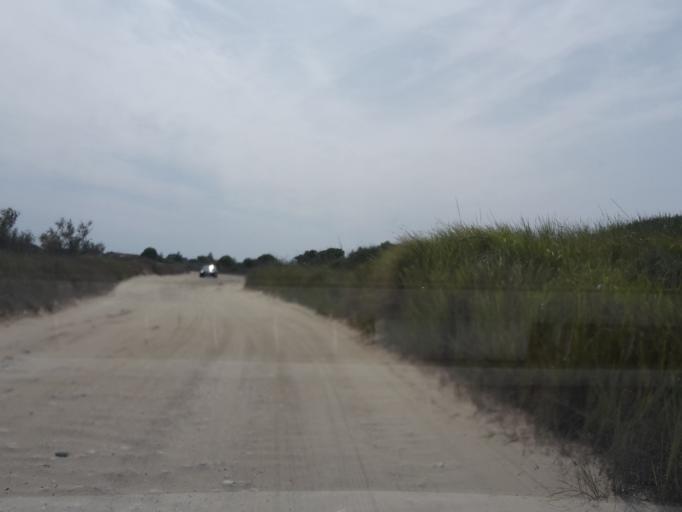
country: FR
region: Provence-Alpes-Cote d'Azur
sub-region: Departement des Bouches-du-Rhone
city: Saintes-Maries-de-la-Mer
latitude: 43.4105
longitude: 4.6071
